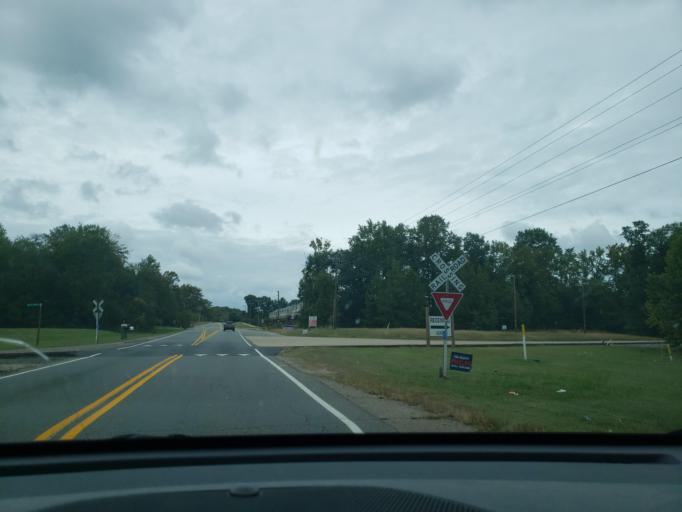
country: US
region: Virginia
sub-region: City of Fredericksburg
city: Fredericksburg
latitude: 38.2399
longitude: -77.4144
